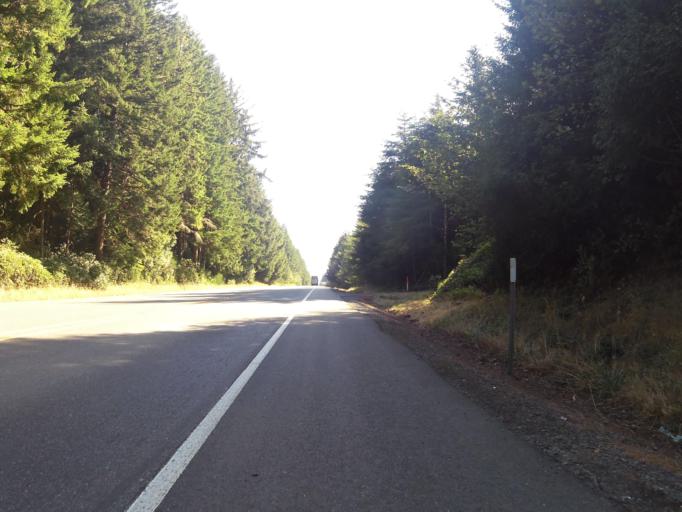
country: US
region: Oregon
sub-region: Coos County
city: Lakeside
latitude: 43.6184
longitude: -124.1814
